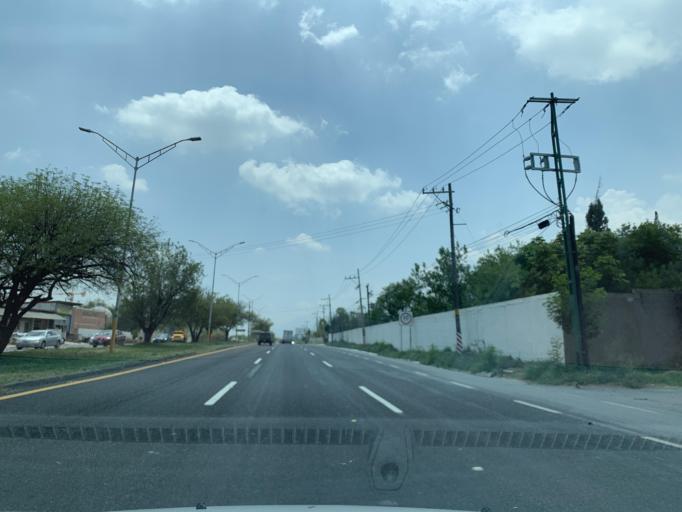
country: MX
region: Nuevo Leon
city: Santiago
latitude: 25.5057
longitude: -100.1934
